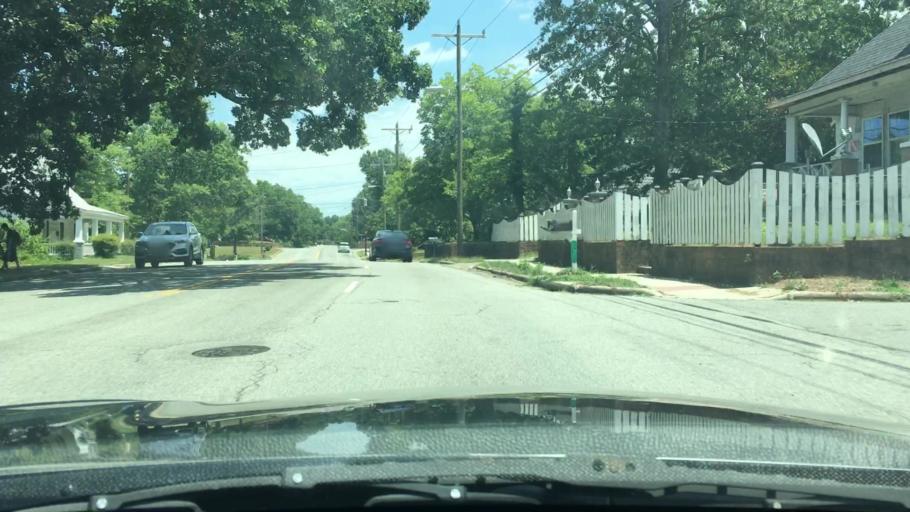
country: US
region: North Carolina
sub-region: Alamance County
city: Burlington
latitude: 36.0923
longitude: -79.4226
